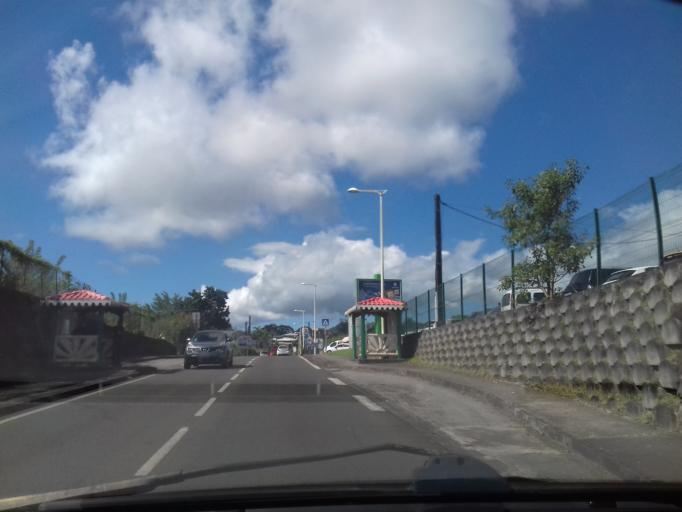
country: MQ
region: Martinique
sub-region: Martinique
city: Saint-Joseph
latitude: 14.6737
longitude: -61.0280
